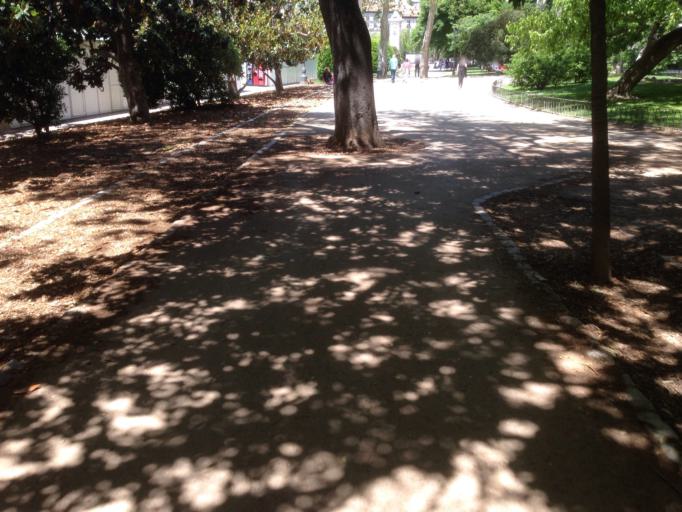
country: ES
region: Madrid
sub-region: Provincia de Madrid
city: Retiro
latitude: 40.4201
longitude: -3.6811
